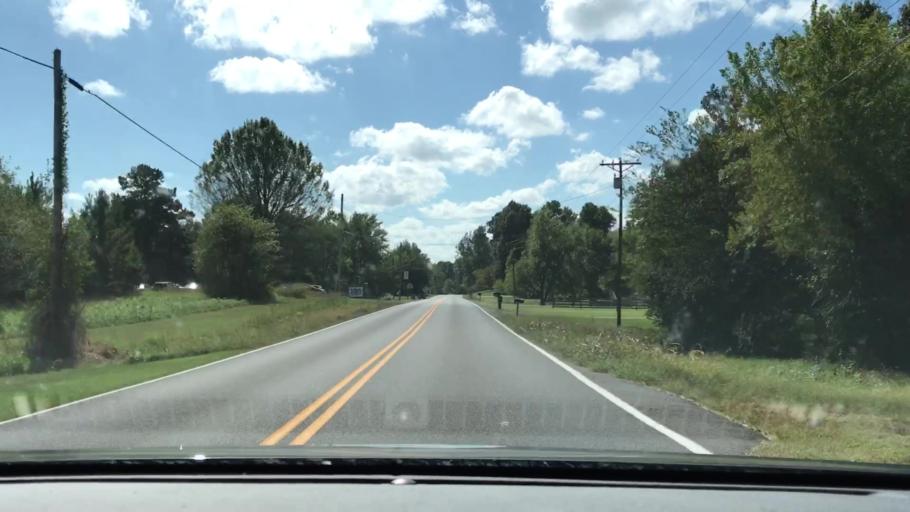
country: US
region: Kentucky
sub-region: McCracken County
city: Reidland
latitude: 36.9155
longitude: -88.5208
